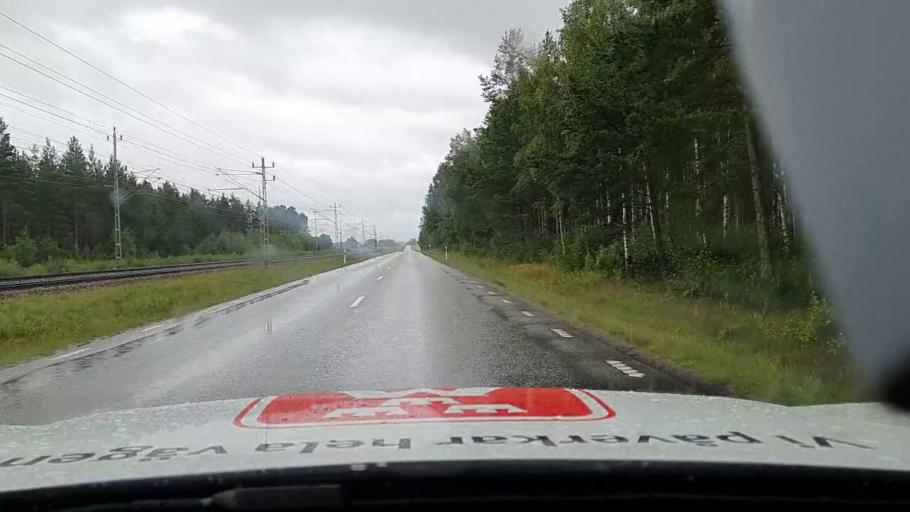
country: SE
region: Vaestra Goetaland
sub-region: Toreboda Kommun
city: Toereboda
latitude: 58.6611
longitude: 14.0878
